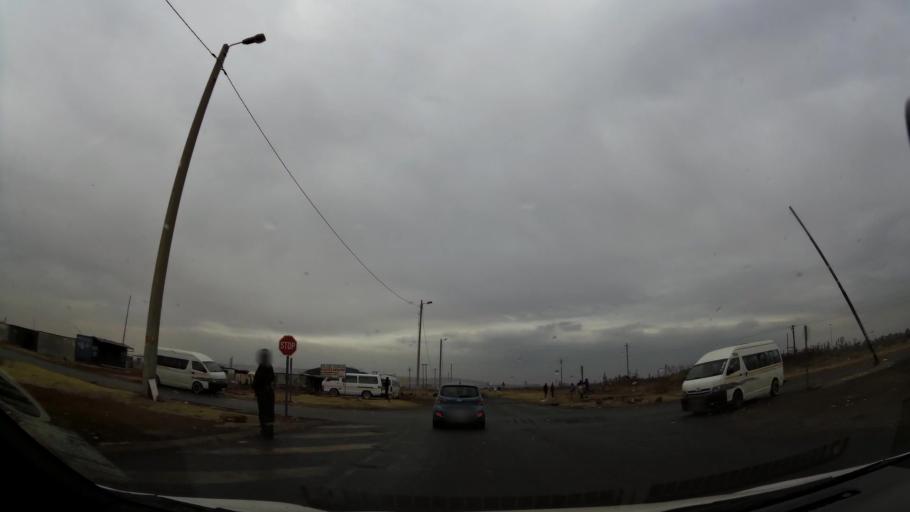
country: ZA
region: Gauteng
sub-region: Ekurhuleni Metropolitan Municipality
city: Germiston
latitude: -26.3850
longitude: 28.1834
